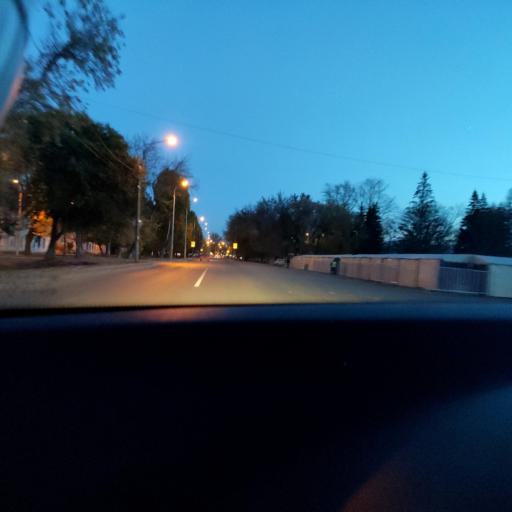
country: RU
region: Samara
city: Petra-Dubrava
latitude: 53.3019
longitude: 50.2834
